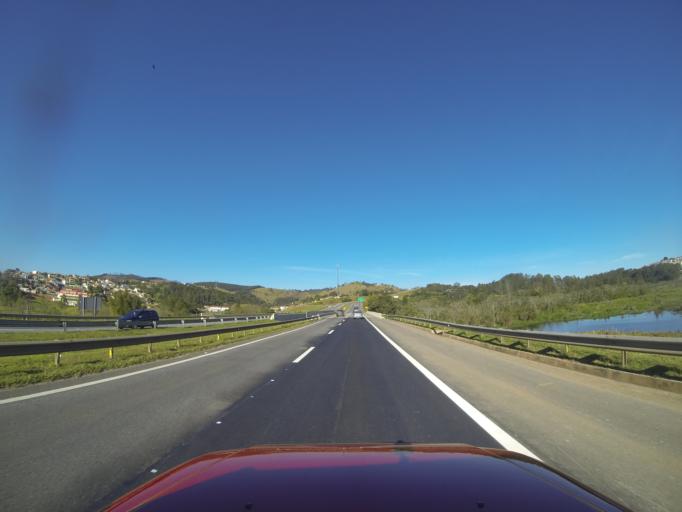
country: BR
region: Sao Paulo
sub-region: Bom Jesus Dos Perdoes
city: Bom Jesus dos Perdoes
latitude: -23.1669
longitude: -46.3995
